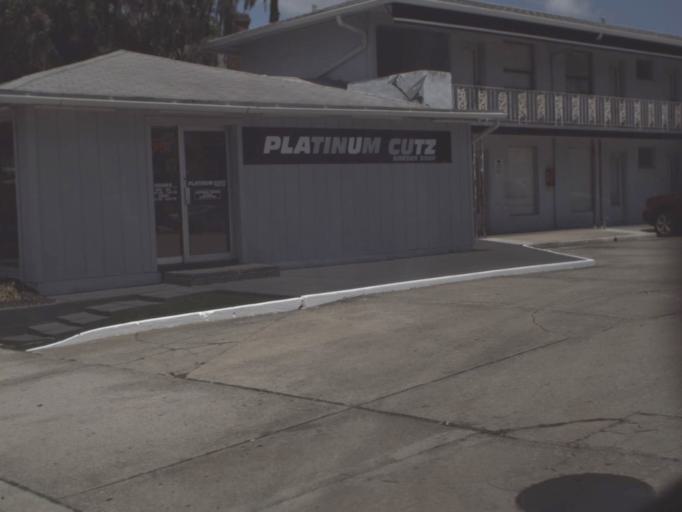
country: US
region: Florida
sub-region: Marion County
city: Ocala
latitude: 29.1871
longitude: -82.1301
